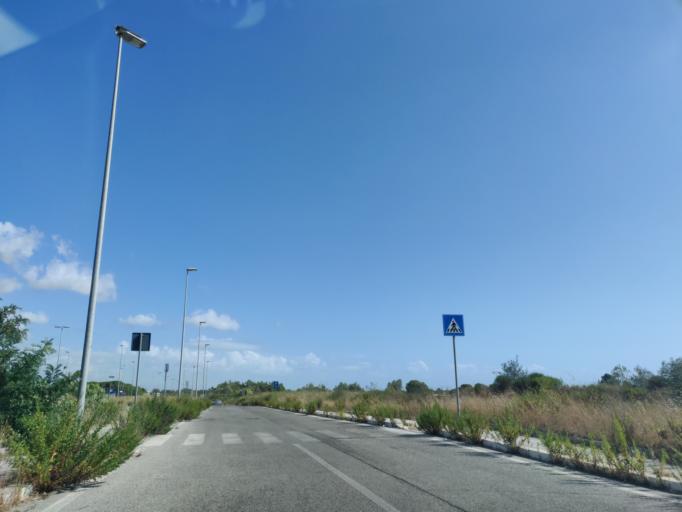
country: IT
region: Latium
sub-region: Citta metropolitana di Roma Capitale
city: Npp 23 (Parco Leonardo)
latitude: 41.7960
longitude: 12.2892
